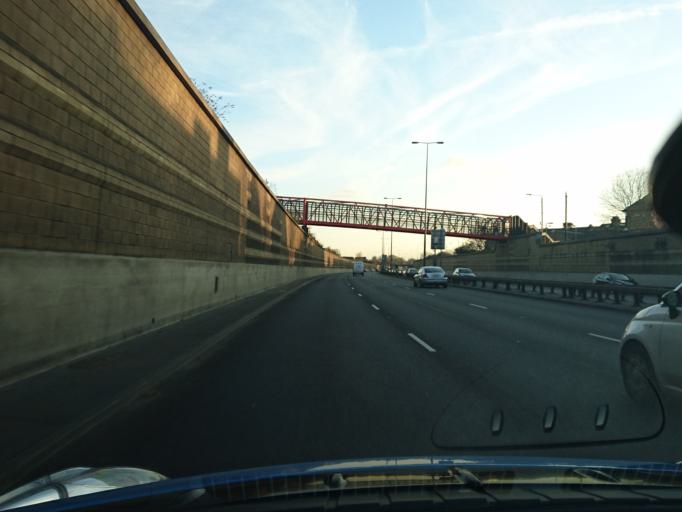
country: GB
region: England
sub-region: Greater London
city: Walthamstow
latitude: 51.5646
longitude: 0.0051
